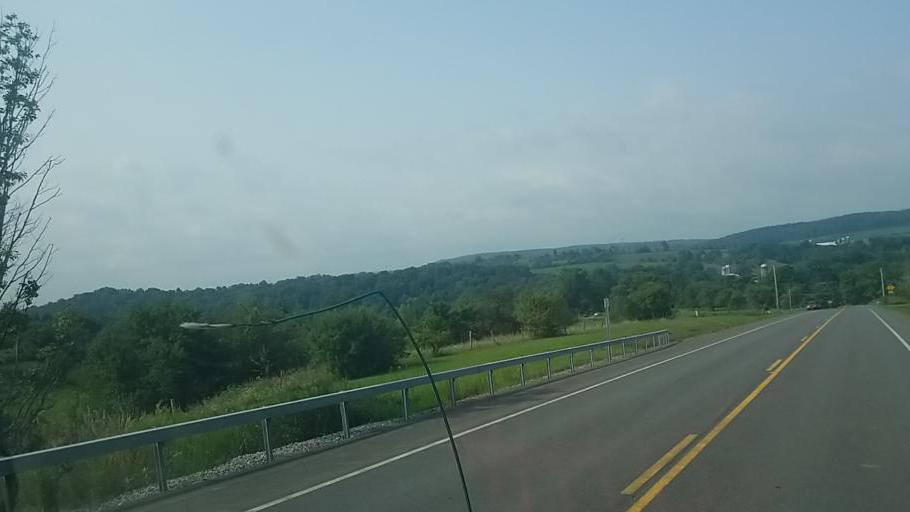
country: US
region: New York
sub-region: Fulton County
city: Johnstown
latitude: 42.9922
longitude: -74.4269
